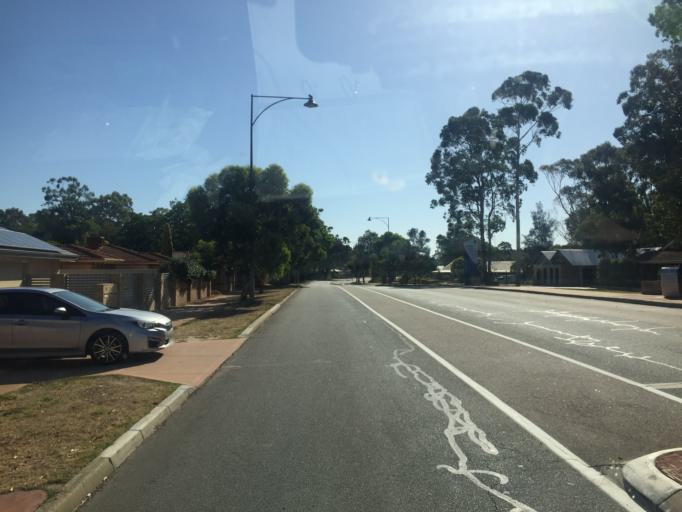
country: AU
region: Western Australia
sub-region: Gosnells
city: Kenwick
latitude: -32.0336
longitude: 115.9803
